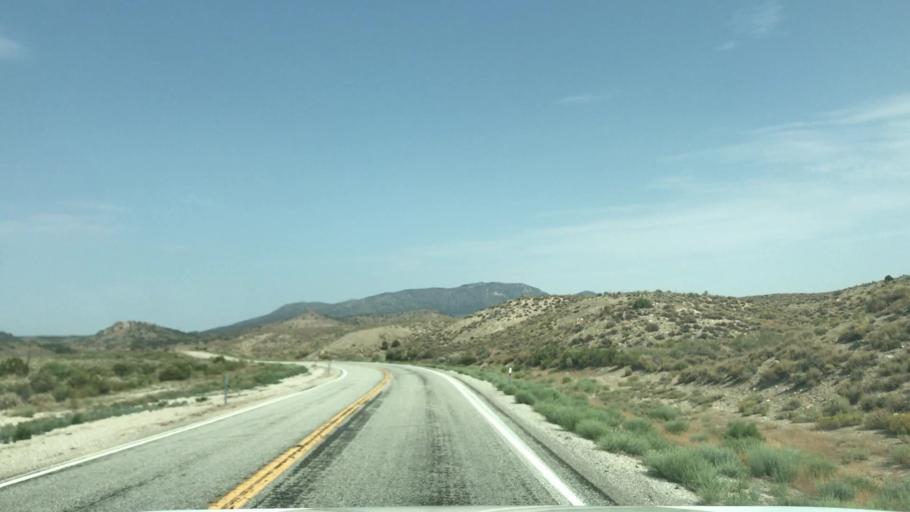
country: US
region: Nevada
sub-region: White Pine County
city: McGill
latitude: 39.1067
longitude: -114.2606
